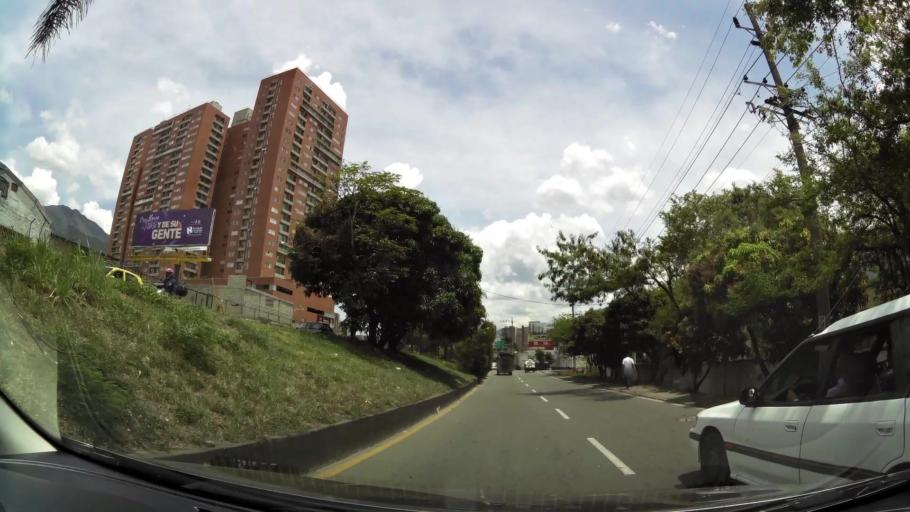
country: CO
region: Antioquia
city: Bello
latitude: 6.3361
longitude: -75.5510
